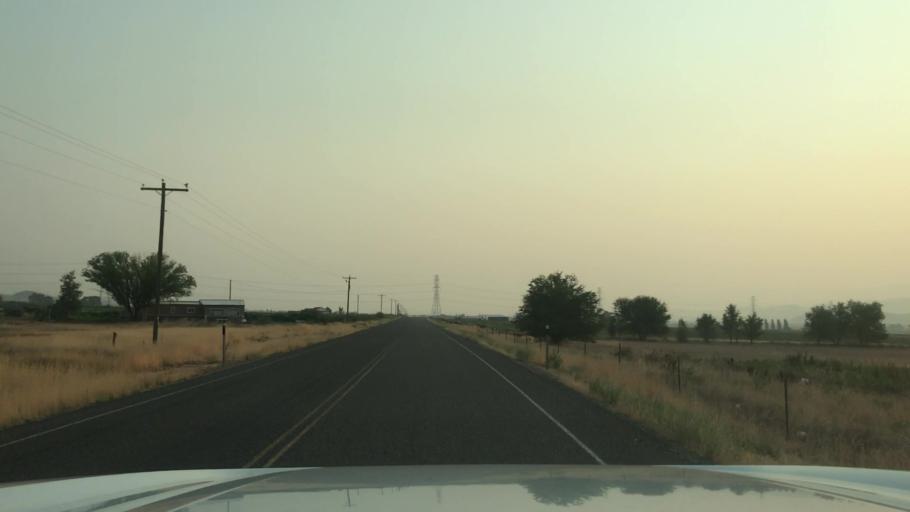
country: US
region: Utah
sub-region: Sevier County
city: Aurora
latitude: 38.8915
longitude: -111.9535
